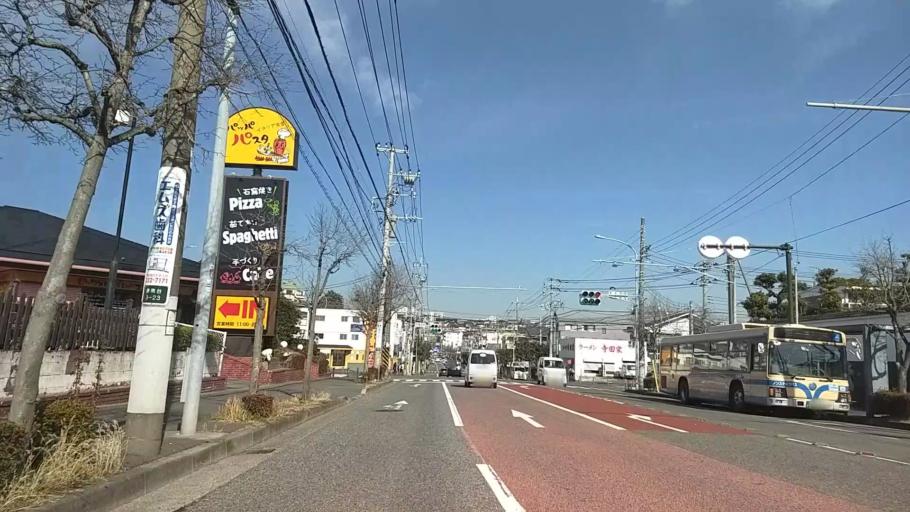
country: JP
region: Kanagawa
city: Kamakura
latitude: 35.3793
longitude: 139.5794
